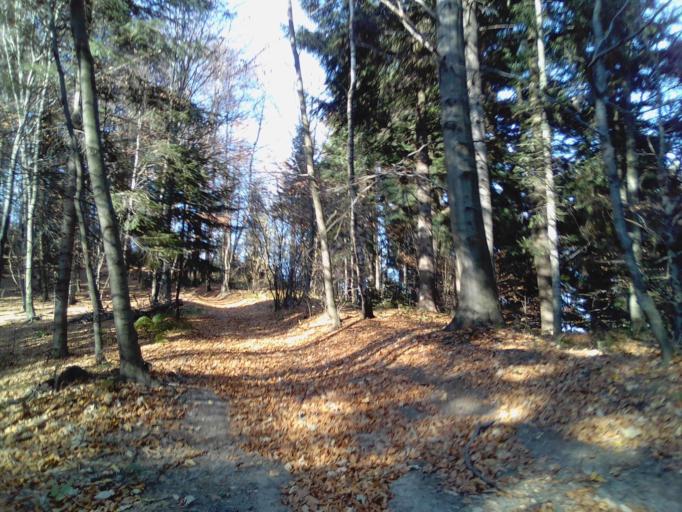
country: PL
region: Subcarpathian Voivodeship
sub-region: Powiat strzyzowski
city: Wysoka Strzyzowska
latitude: 49.8141
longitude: 21.7133
